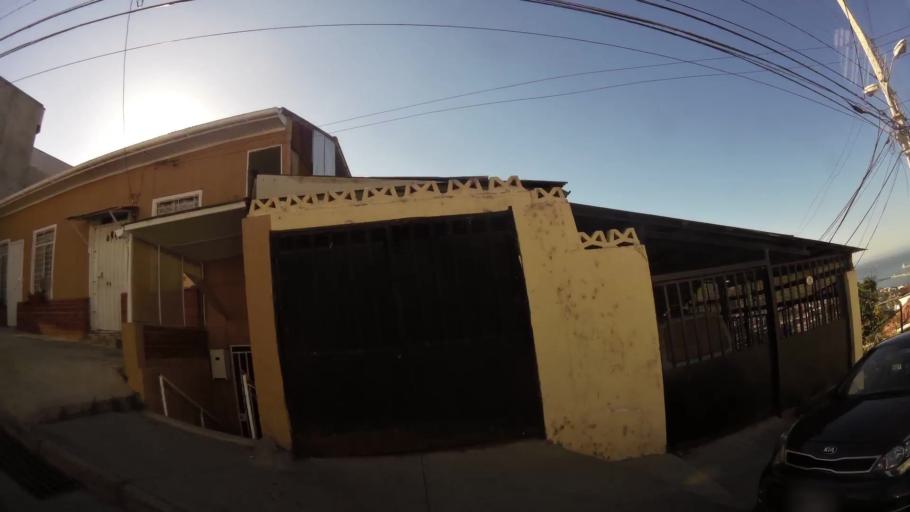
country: CL
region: Valparaiso
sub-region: Provincia de Valparaiso
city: Valparaiso
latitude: -33.0545
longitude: -71.6252
